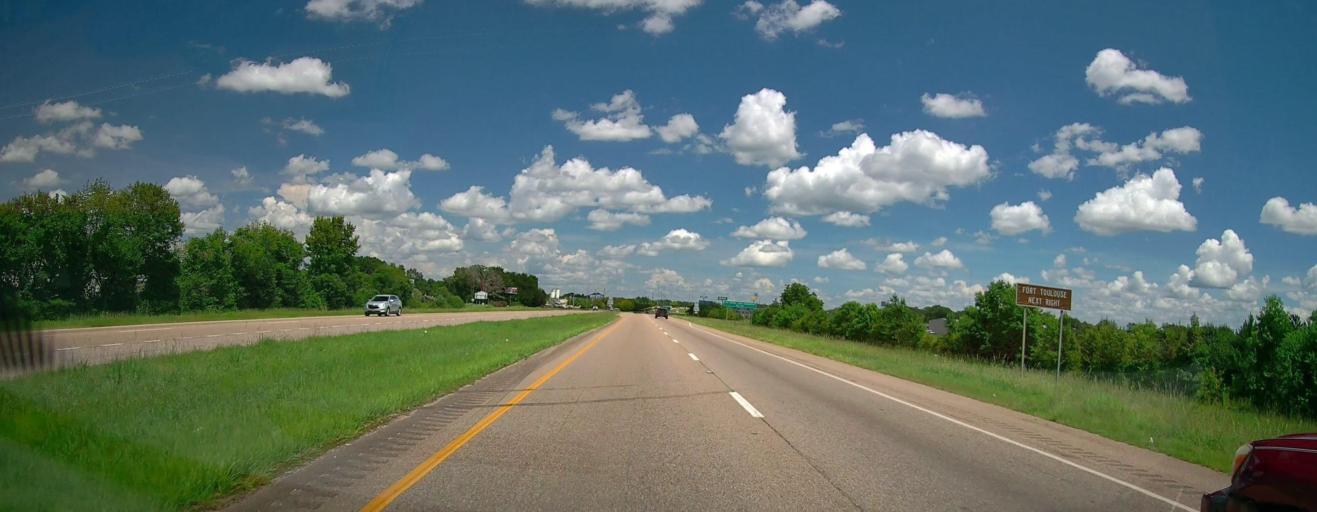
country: US
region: Alabama
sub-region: Montgomery County
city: Montgomery
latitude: 32.4218
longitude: -86.2393
